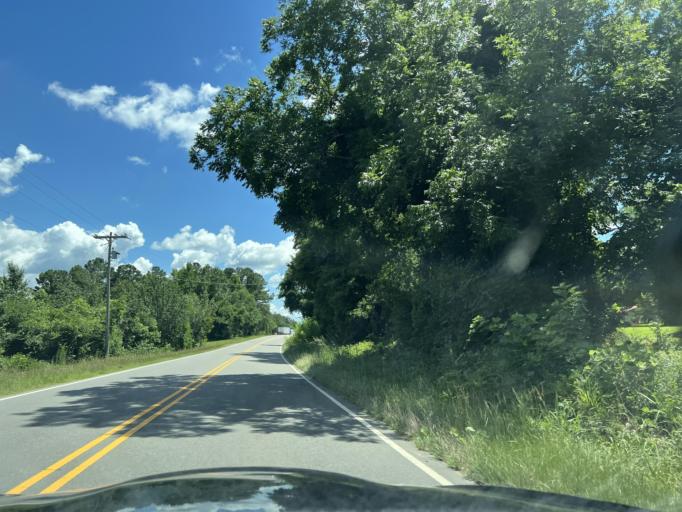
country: US
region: North Carolina
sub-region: Lee County
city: Sanford
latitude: 35.4489
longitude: -79.1712
